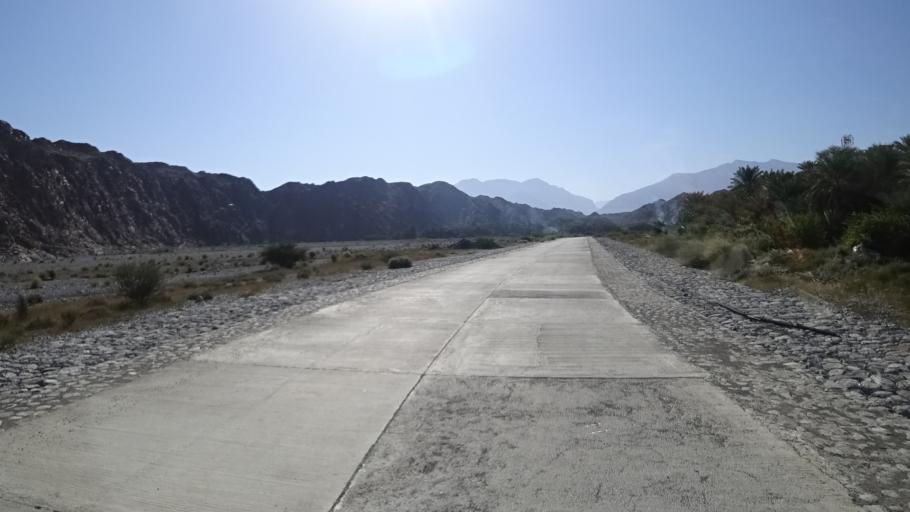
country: OM
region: Al Batinah
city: Bayt al `Awabi
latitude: 23.3837
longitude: 57.6620
